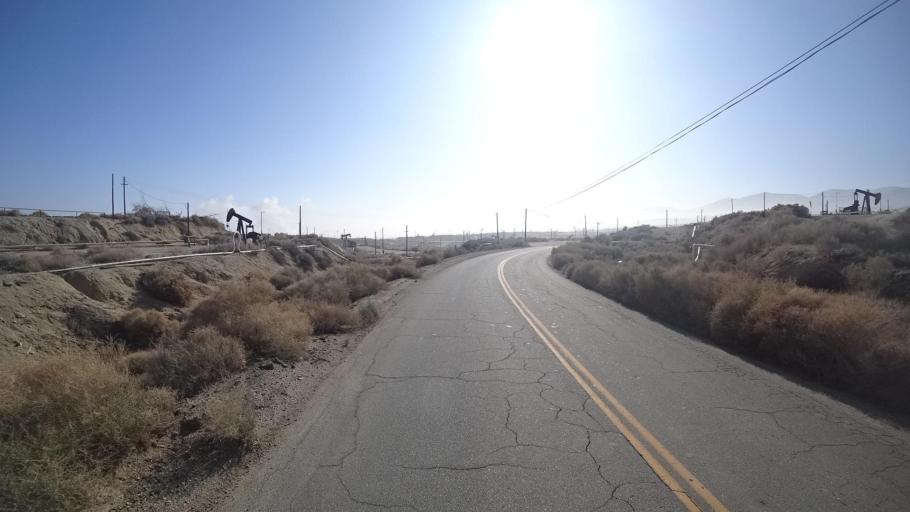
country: US
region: California
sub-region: Kern County
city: Taft Heights
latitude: 35.2218
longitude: -119.6097
